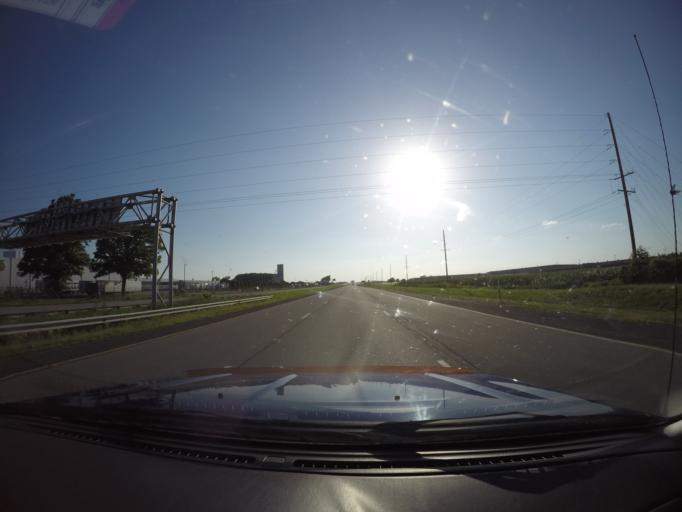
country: US
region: Kansas
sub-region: Shawnee County
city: Topeka
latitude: 39.0907
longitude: -95.7340
